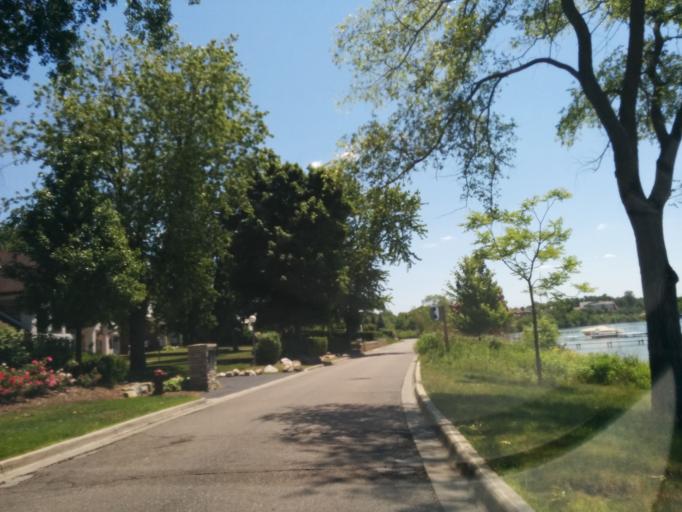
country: US
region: Michigan
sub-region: Oakland County
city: Orchard Lake
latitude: 42.5884
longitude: -83.3563
